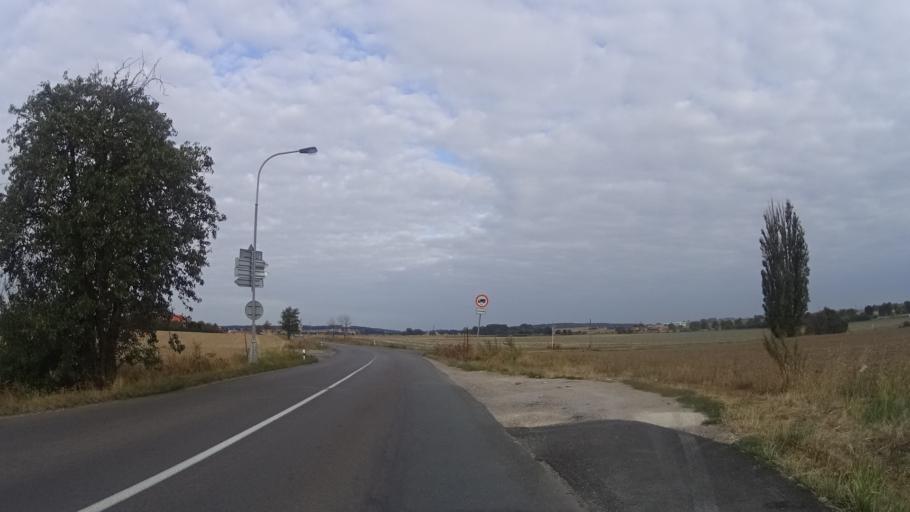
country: CZ
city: Stezery
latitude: 50.2105
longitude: 15.7807
